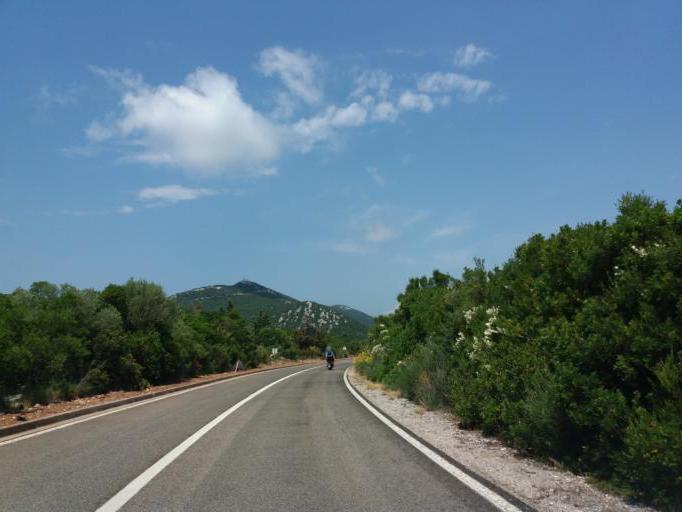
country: HR
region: Zadarska
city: Sali
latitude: 43.9812
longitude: 15.0770
